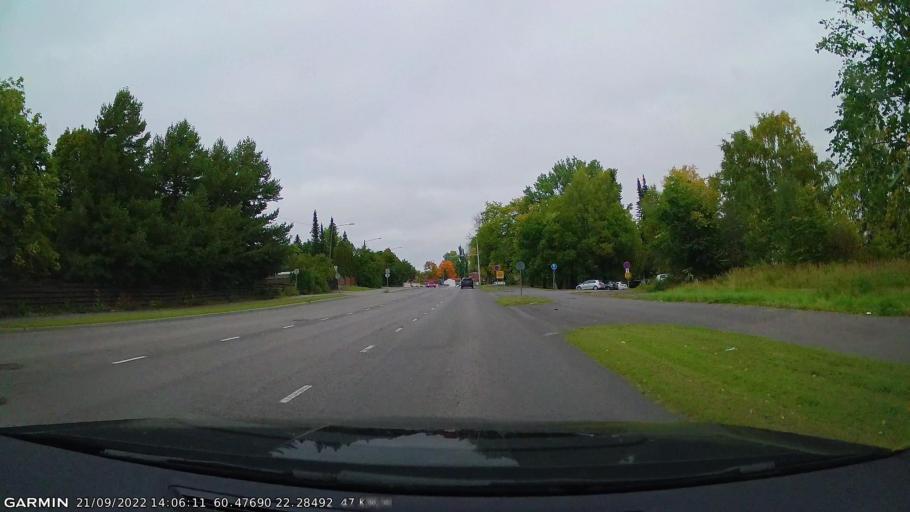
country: FI
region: Varsinais-Suomi
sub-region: Turku
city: Turku
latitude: 60.4768
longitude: 22.2847
